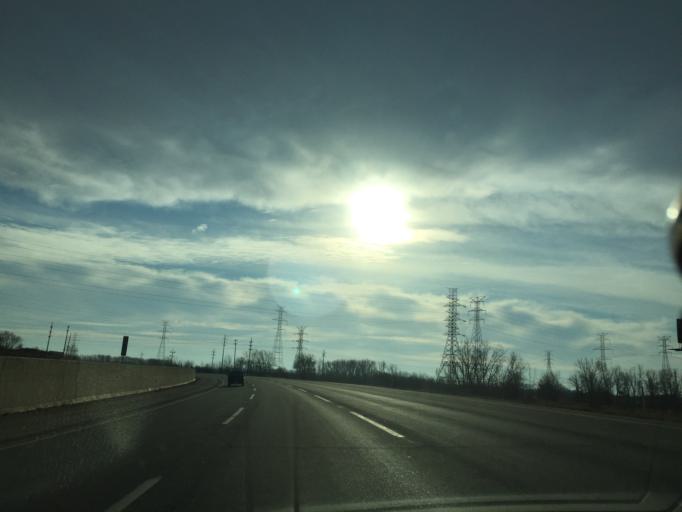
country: US
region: Indiana
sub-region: Lake County
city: New Chicago
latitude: 41.5864
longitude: -87.3014
